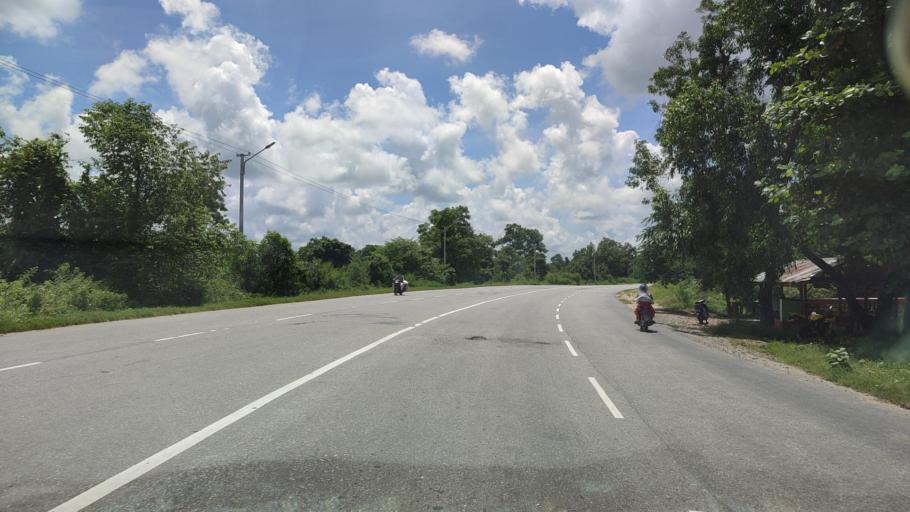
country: MM
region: Bago
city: Taungoo
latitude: 18.9612
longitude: 96.4338
